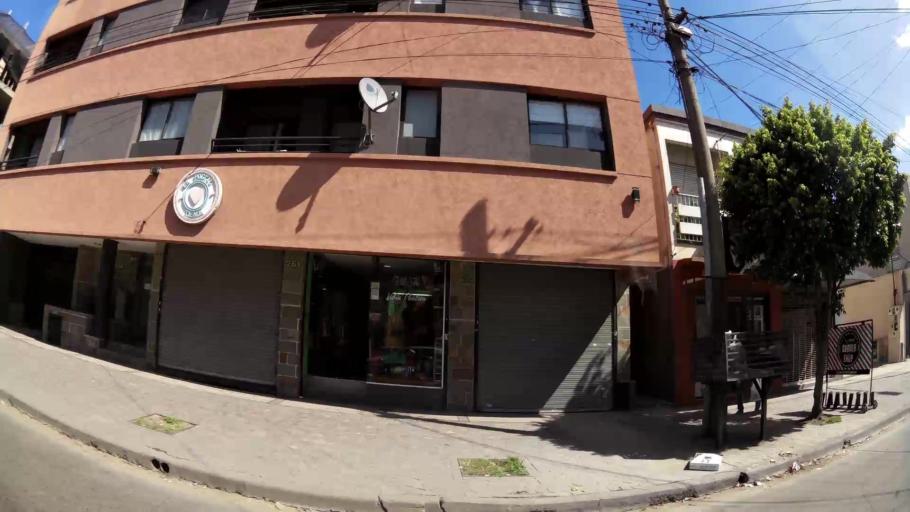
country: AR
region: Buenos Aires
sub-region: Partido de Quilmes
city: Quilmes
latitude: -34.8078
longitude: -58.2736
